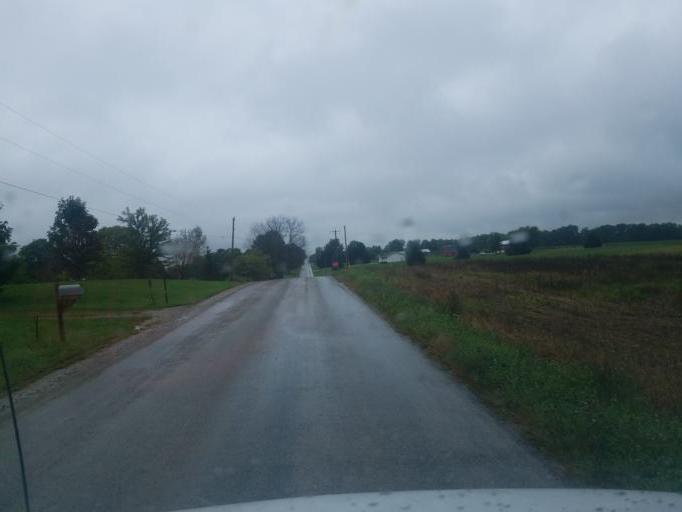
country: US
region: Ohio
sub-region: Wayne County
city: West Salem
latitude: 40.9377
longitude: -82.0561
